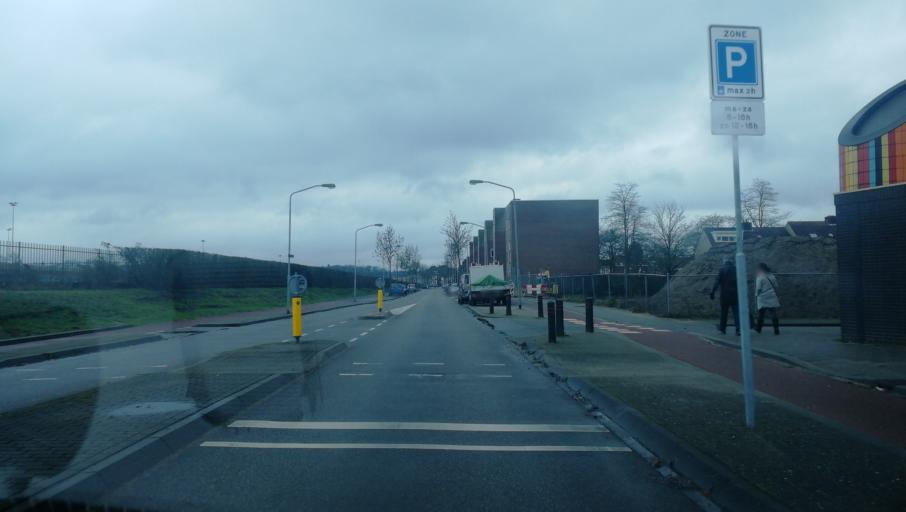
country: NL
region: Limburg
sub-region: Gemeente Venlo
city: Venlo
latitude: 51.3646
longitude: 6.1682
